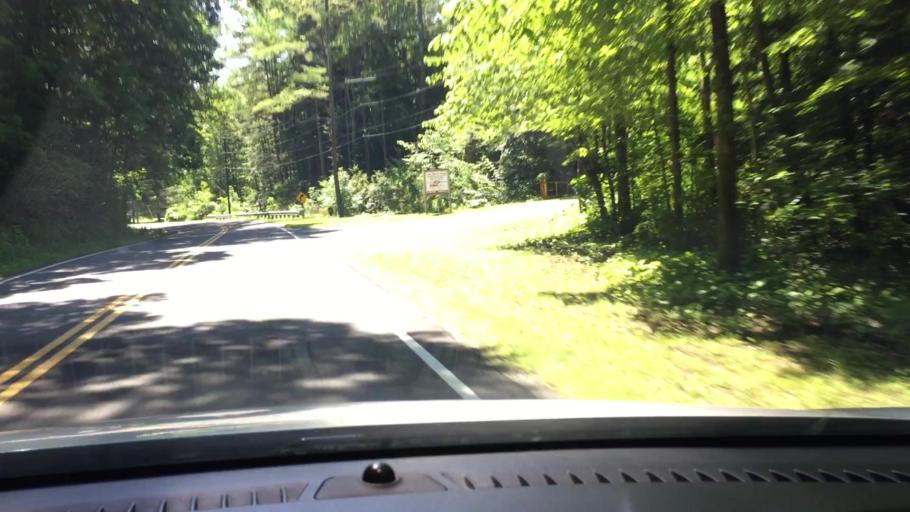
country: US
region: Massachusetts
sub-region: Berkshire County
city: Lenox
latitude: 42.3512
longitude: -73.2469
